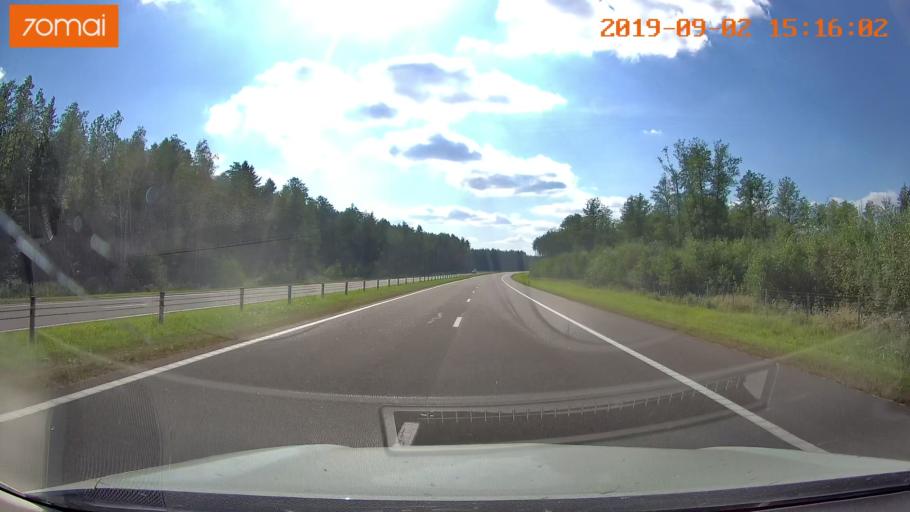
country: BY
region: Mogilev
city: Byalynichy
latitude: 53.9442
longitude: 29.6347
